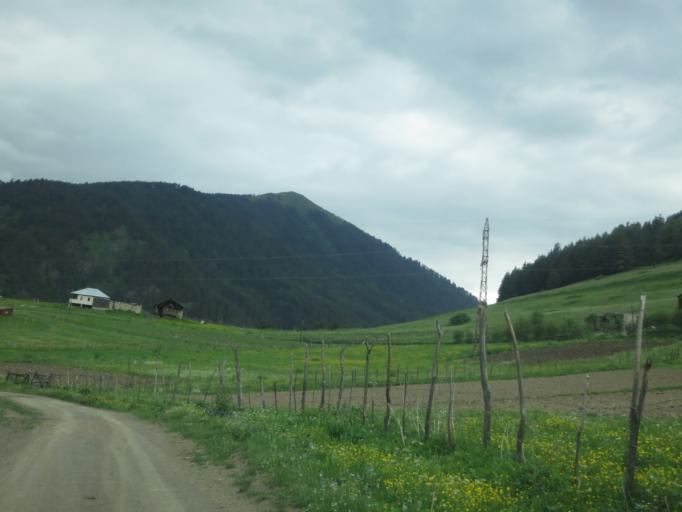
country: RU
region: Chechnya
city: Itum-Kali
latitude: 42.3695
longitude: 45.6296
